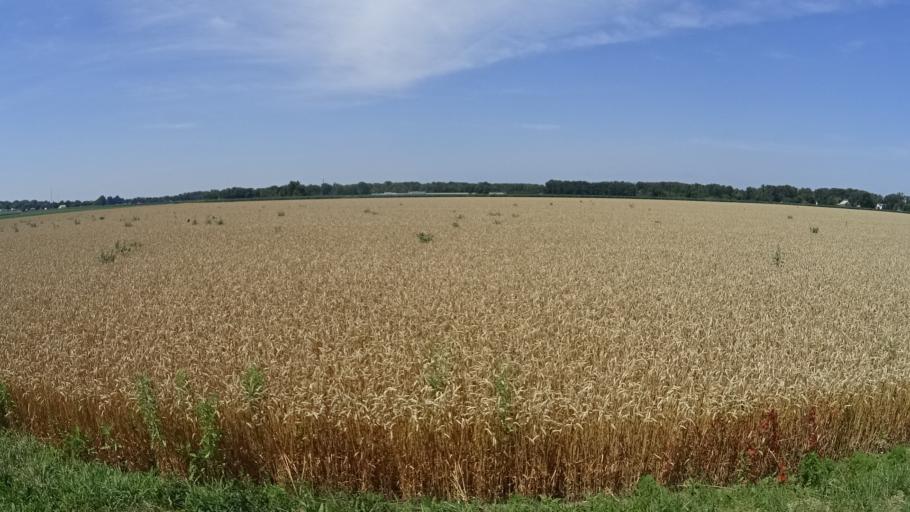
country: US
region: Ohio
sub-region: Erie County
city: Sandusky
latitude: 41.4178
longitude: -82.7894
